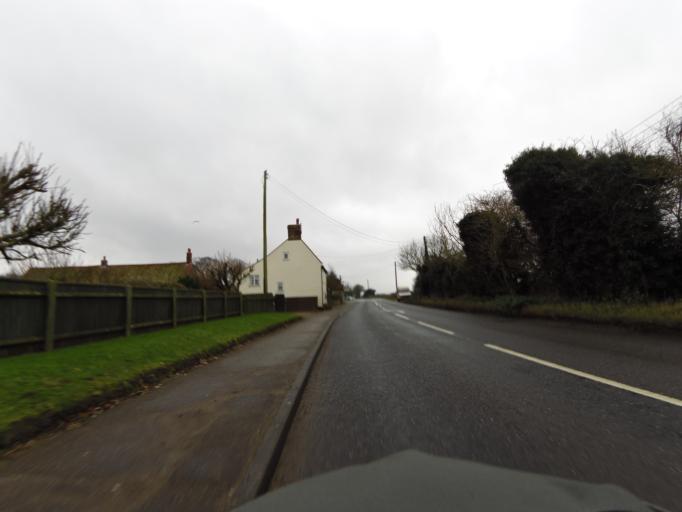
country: GB
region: England
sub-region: Norfolk
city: Briston
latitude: 52.8996
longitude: 1.0892
